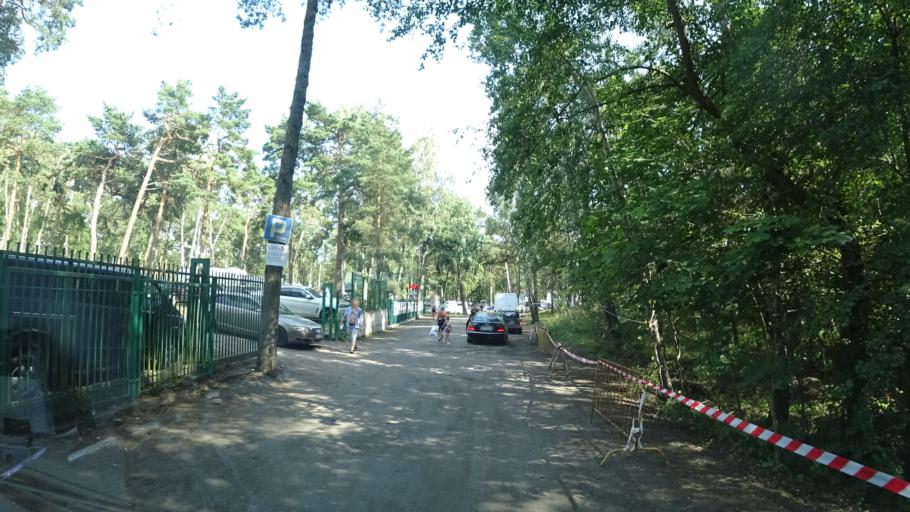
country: PL
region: Pomeranian Voivodeship
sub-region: Gdansk
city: Gdansk
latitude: 54.3709
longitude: 18.7288
